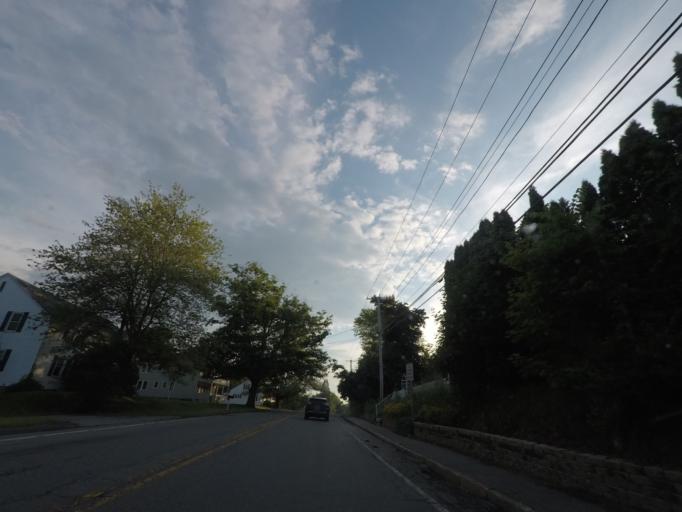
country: US
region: Massachusetts
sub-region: Worcester County
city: Fiskdale
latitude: 42.1138
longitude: -72.1199
